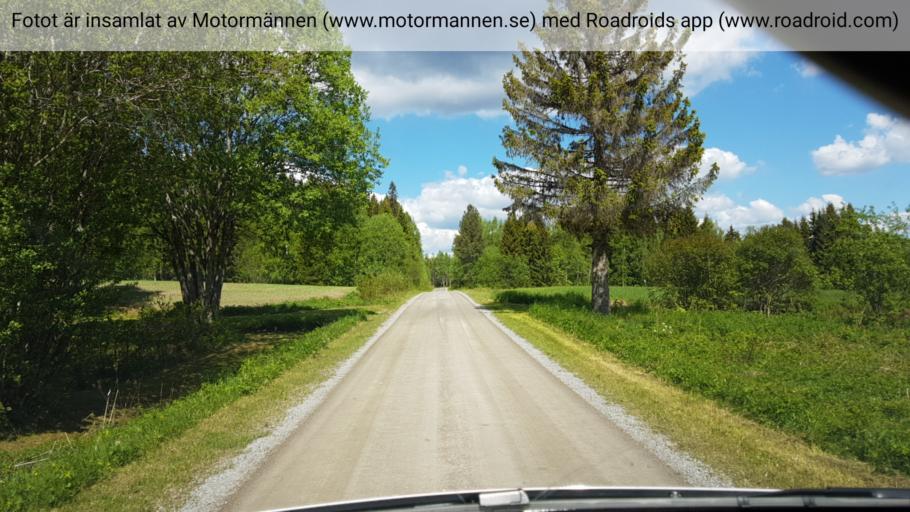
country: SE
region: Jaemtland
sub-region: OEstersunds Kommun
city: Brunflo
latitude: 63.0223
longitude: 15.0754
